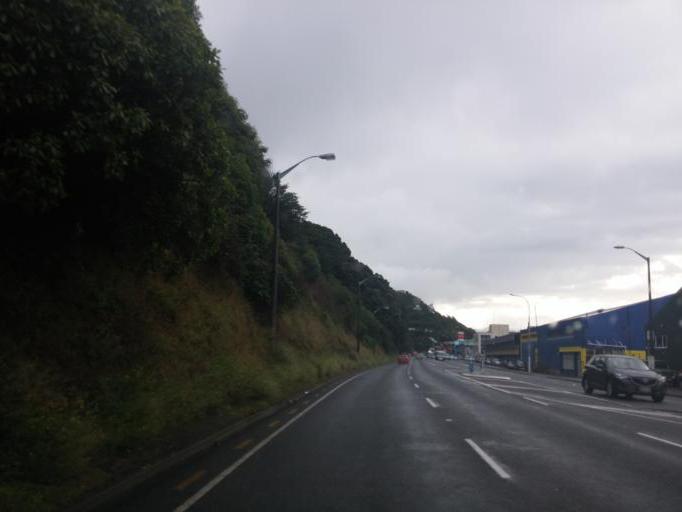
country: NZ
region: Wellington
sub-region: Wellington City
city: Wellington
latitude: -41.2585
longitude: 174.7916
